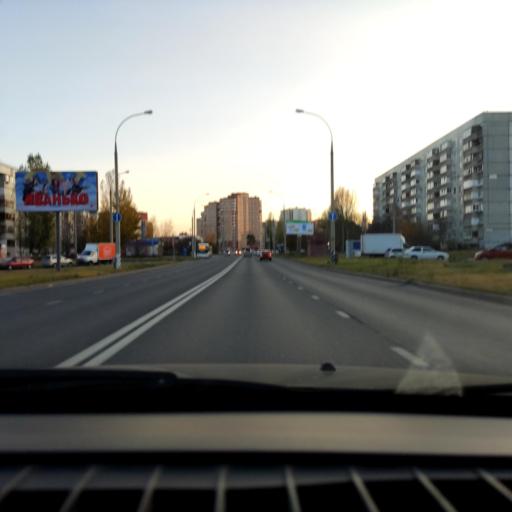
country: RU
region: Samara
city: Tol'yatti
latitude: 53.5428
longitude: 49.3607
